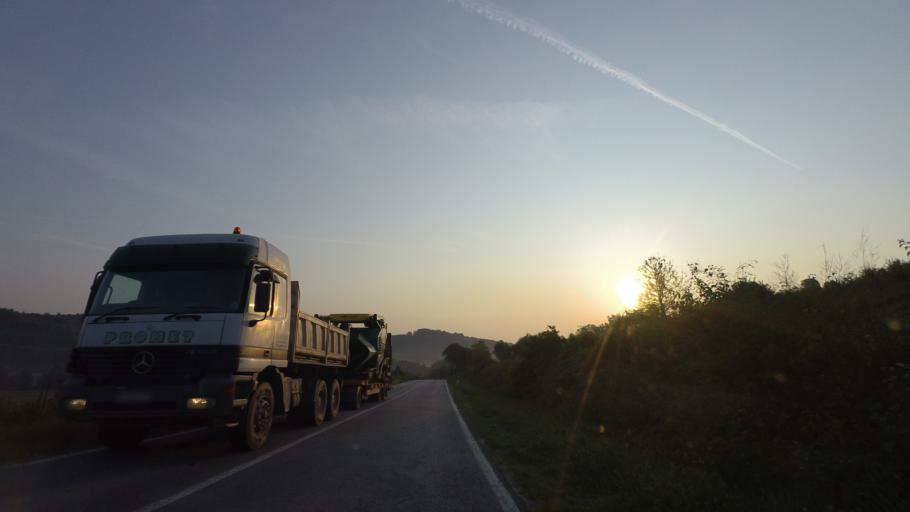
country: HR
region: Brodsko-Posavska
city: Resetari
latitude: 45.3420
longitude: 17.4609
